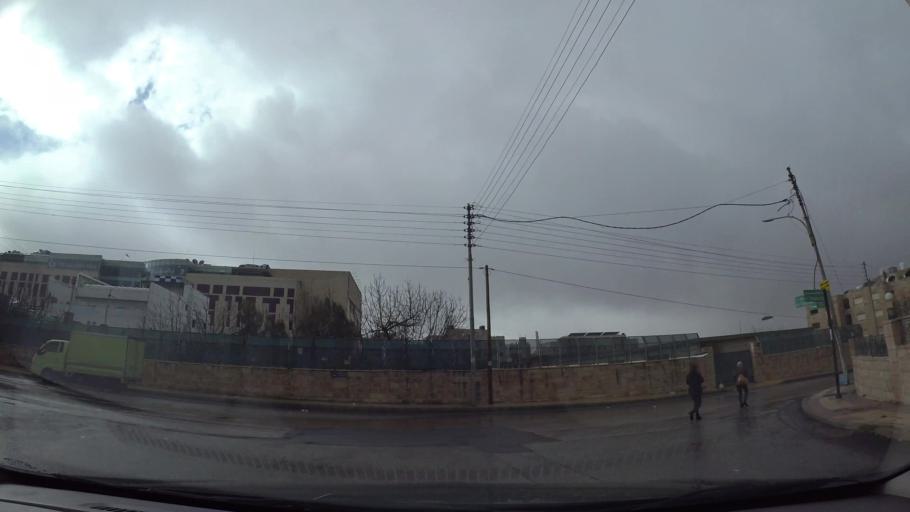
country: JO
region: Amman
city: Wadi as Sir
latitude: 31.9607
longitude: 35.8613
